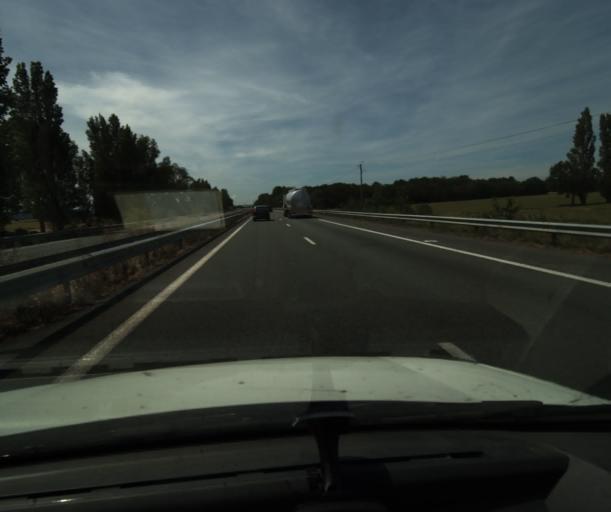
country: FR
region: Languedoc-Roussillon
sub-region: Departement de l'Aude
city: Villepinte
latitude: 43.2455
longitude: 2.0727
